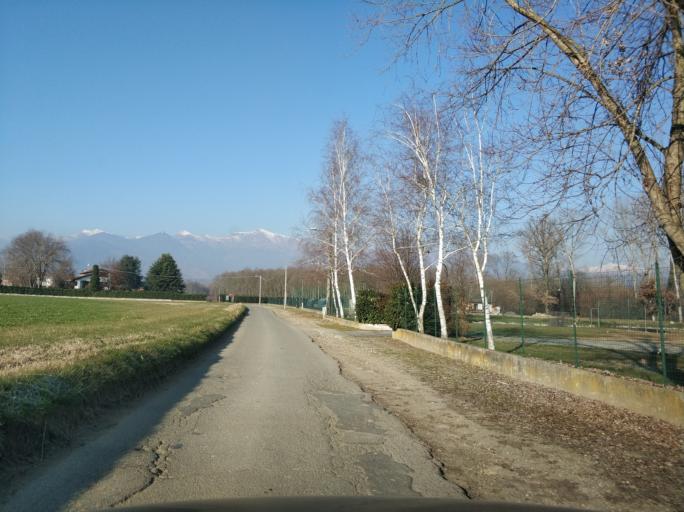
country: IT
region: Piedmont
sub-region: Provincia di Torino
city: Barbania
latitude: 45.3085
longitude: 7.6429
